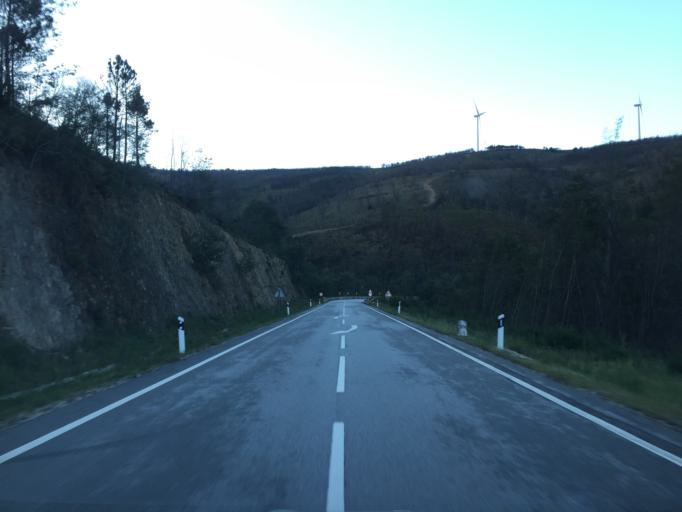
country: PT
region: Coimbra
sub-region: Pampilhosa da Serra
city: Pampilhosa da Serra
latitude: 40.1011
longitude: -7.9896
